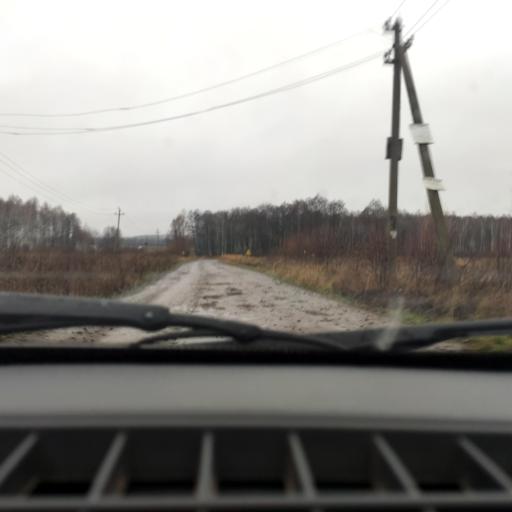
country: RU
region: Bashkortostan
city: Avdon
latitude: 54.6323
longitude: 55.7325
